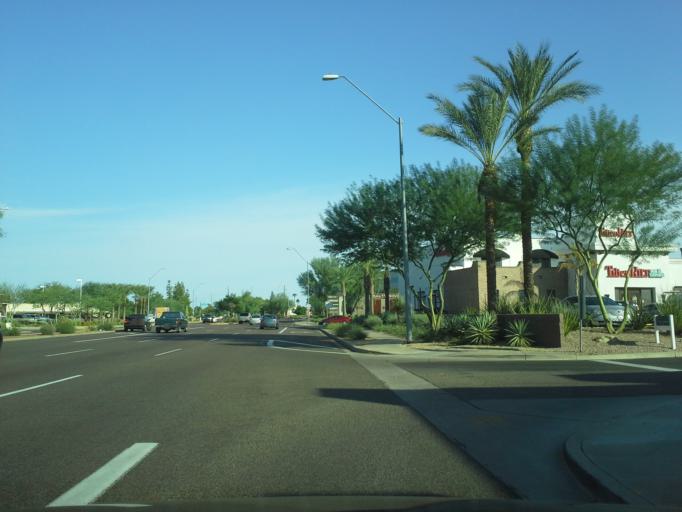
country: US
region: Arizona
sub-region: Maricopa County
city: Paradise Valley
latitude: 33.5981
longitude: -111.9791
